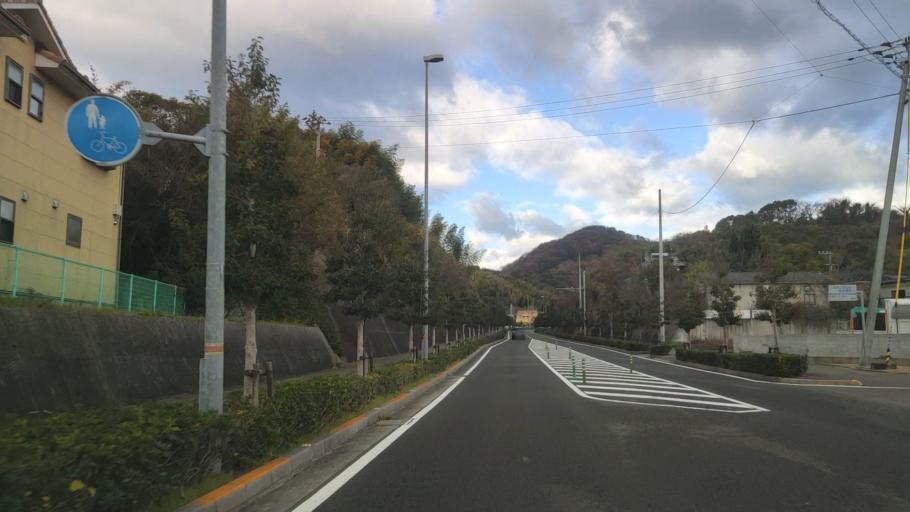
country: JP
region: Ehime
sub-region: Shikoku-chuo Shi
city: Matsuyama
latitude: 33.8734
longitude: 132.7175
